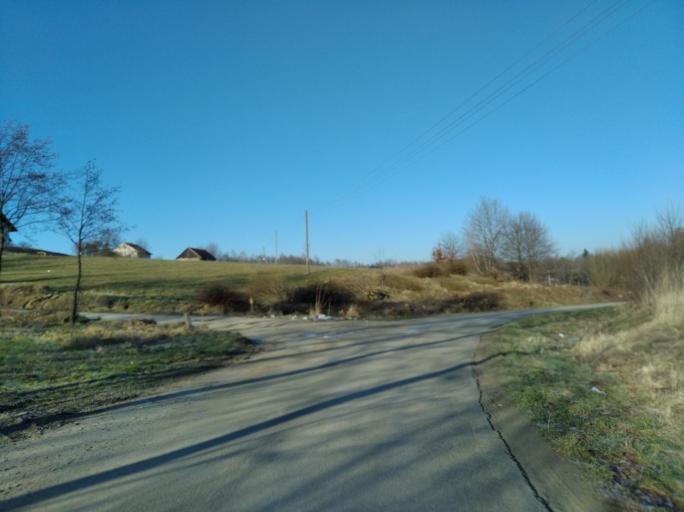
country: PL
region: Subcarpathian Voivodeship
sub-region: Powiat strzyzowski
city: Wysoka Strzyzowska
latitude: 49.8472
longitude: 21.7617
